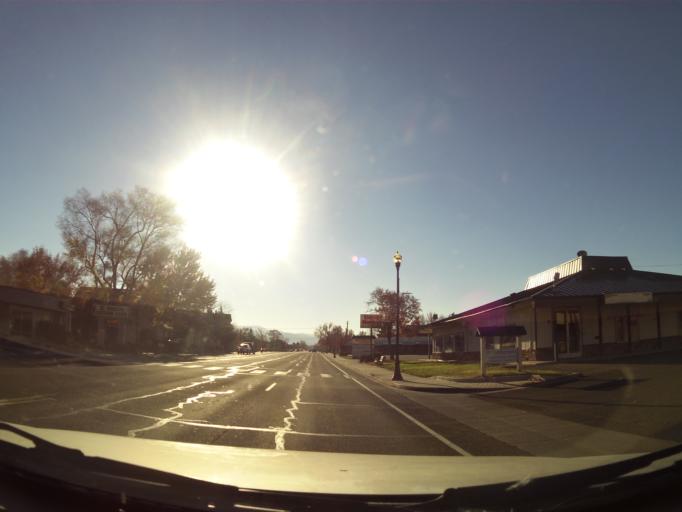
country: US
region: Nevada
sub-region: Douglas County
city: Minden
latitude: 38.9479
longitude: -119.7577
